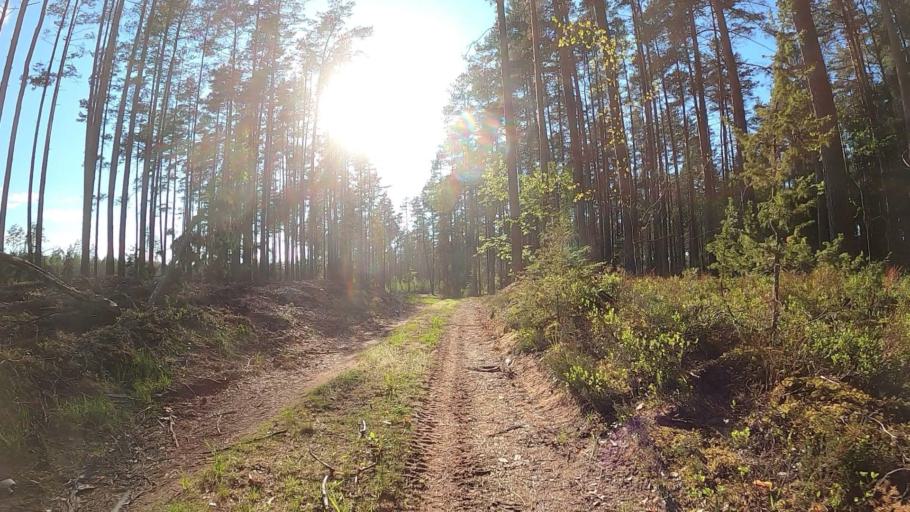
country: LV
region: Baldone
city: Baldone
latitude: 56.7674
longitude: 24.3650
